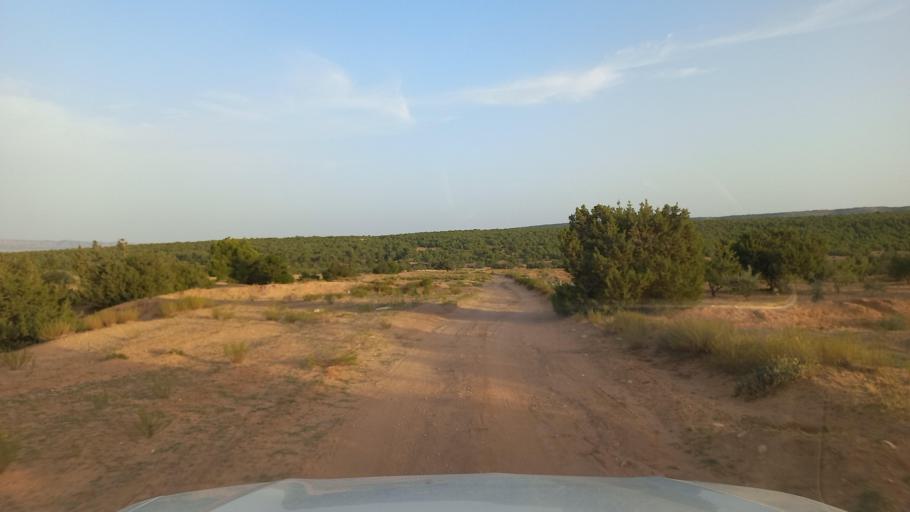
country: TN
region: Al Qasrayn
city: Sbiba
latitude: 35.4116
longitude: 8.9126
